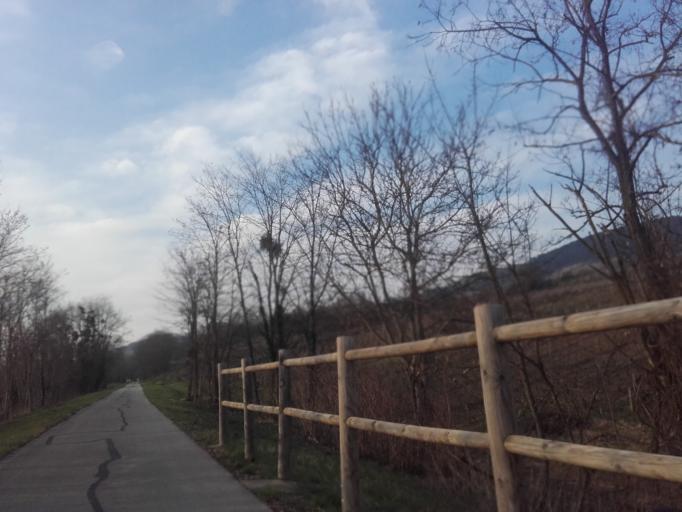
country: FR
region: Bourgogne
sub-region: Departement de la Cote-d'Or
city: Nolay
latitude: 46.9040
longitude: 4.6639
